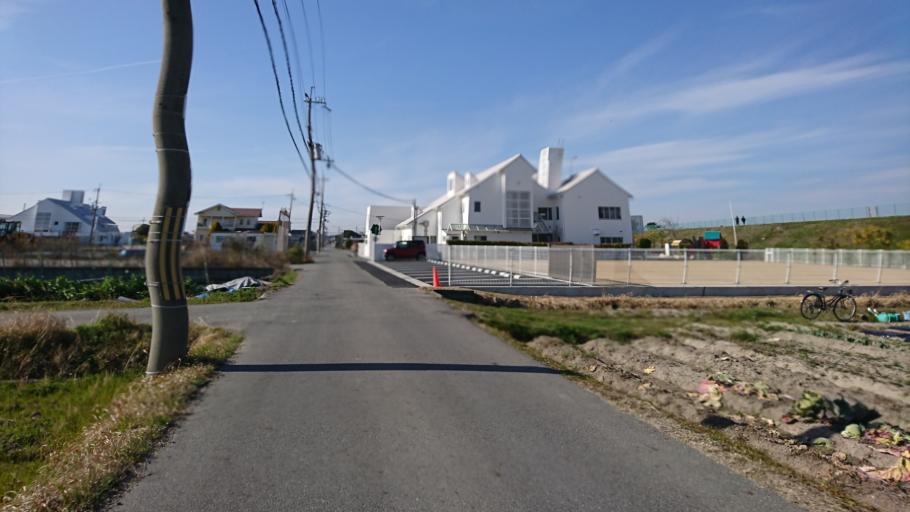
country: JP
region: Hyogo
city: Kakogawacho-honmachi
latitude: 34.7288
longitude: 134.8751
